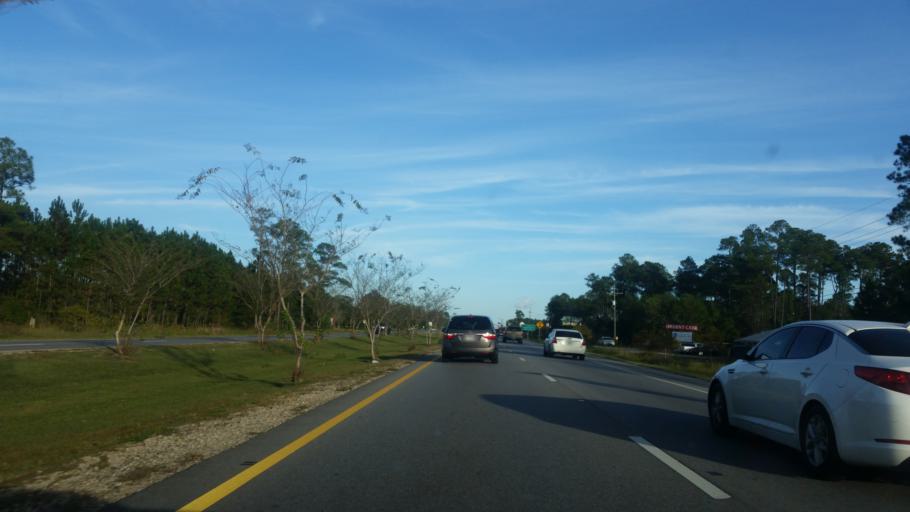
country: US
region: Mississippi
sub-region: Jackson County
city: Gulf Park Estates
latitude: 30.4033
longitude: -88.7247
